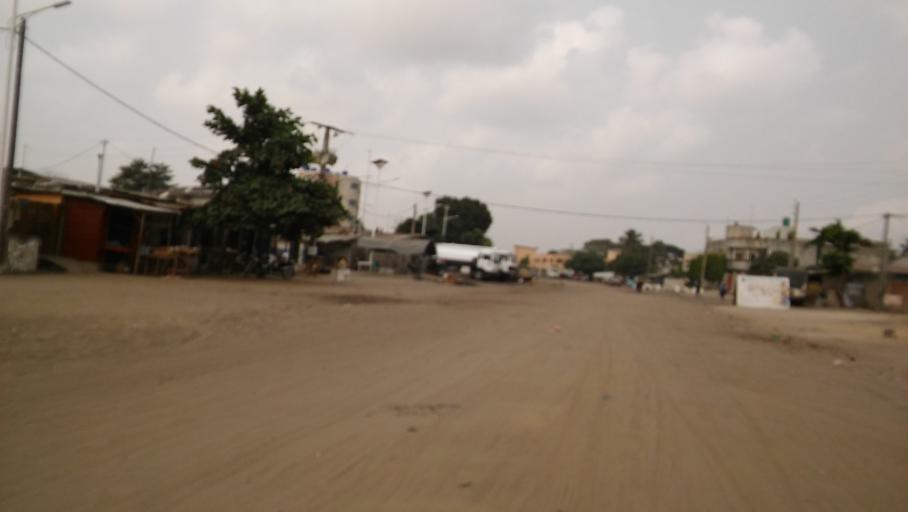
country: BJ
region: Littoral
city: Cotonou
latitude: 6.3906
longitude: 2.3813
